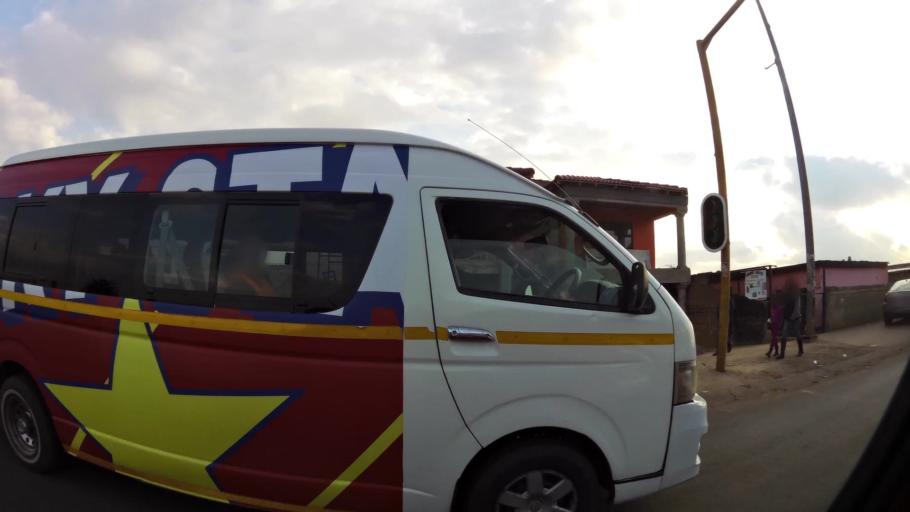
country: ZA
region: Gauteng
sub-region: City of Johannesburg Metropolitan Municipality
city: Orange Farm
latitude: -26.5725
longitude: 27.8383
